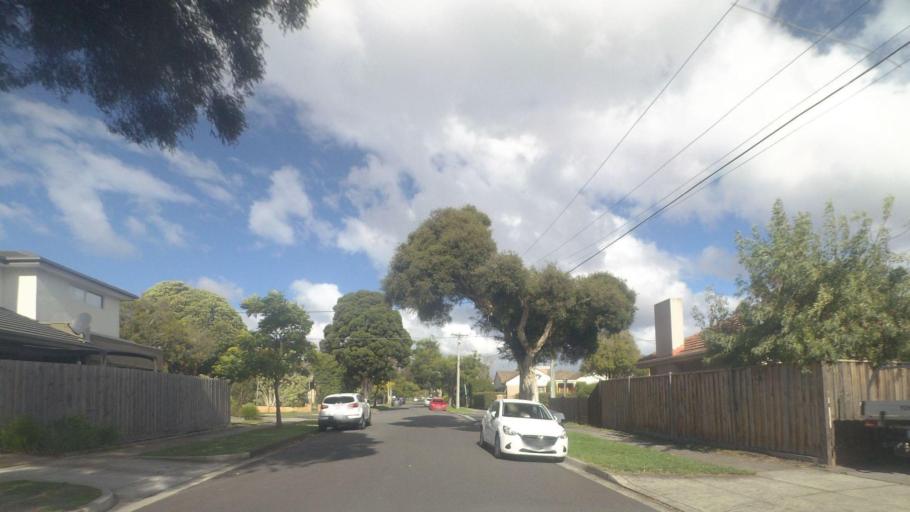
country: AU
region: Victoria
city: Forest Hill
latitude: -37.8404
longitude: 145.1775
